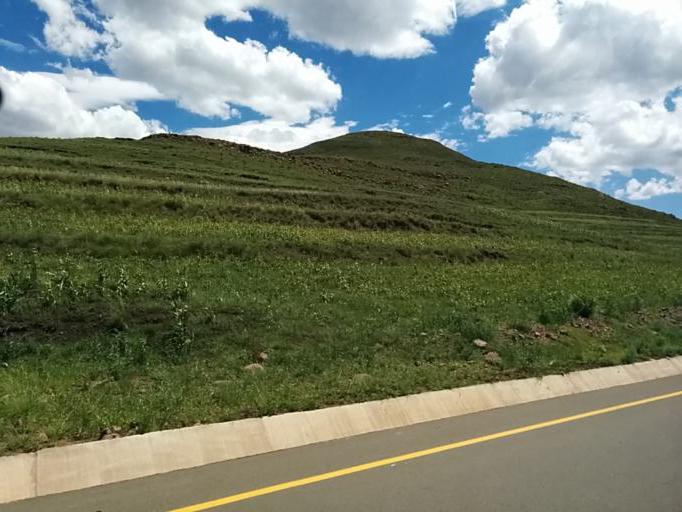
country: LS
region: Maseru
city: Nako
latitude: -29.9612
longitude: 28.1626
